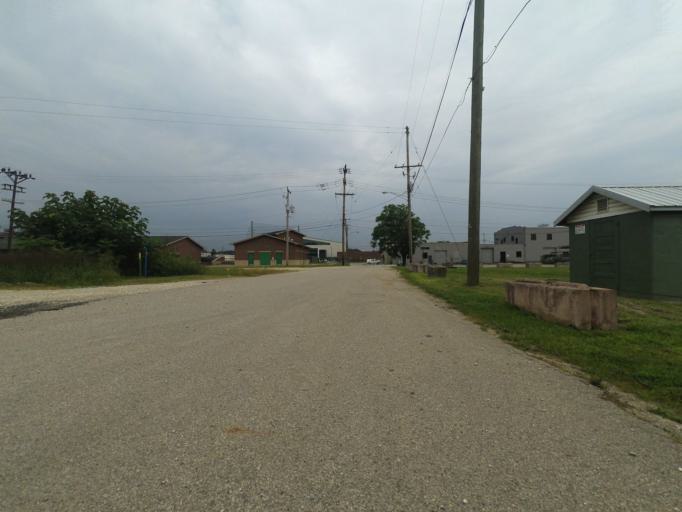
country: US
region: West Virginia
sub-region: Cabell County
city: Huntington
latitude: 38.4278
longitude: -82.4203
